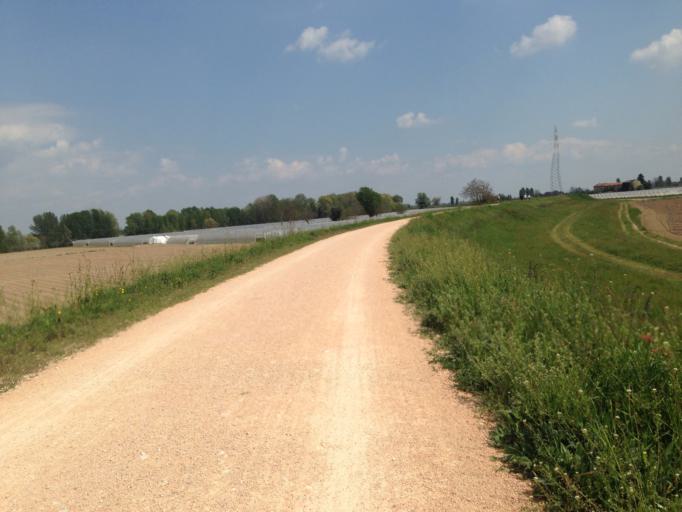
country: IT
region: Veneto
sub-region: Provincia di Verona
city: Campagnola
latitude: 45.3845
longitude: 11.0792
